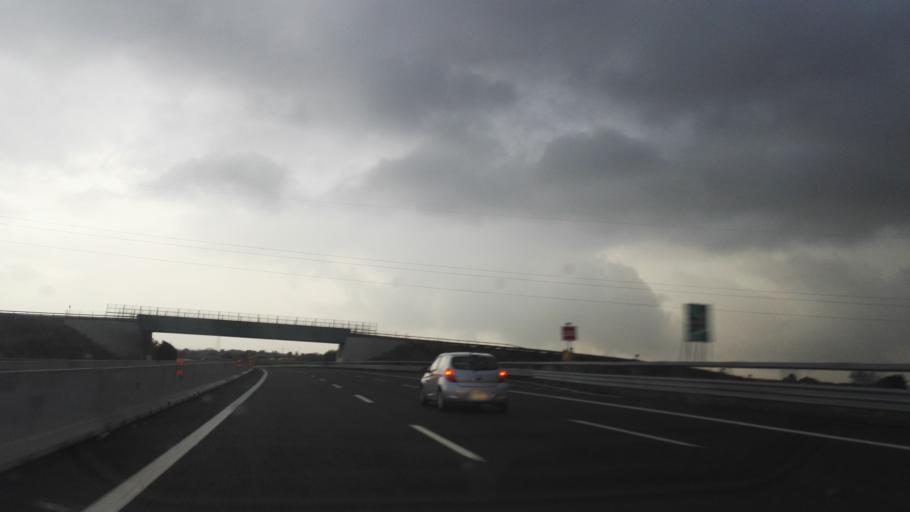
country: IT
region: Lombardy
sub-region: Citta metropolitana di Milano
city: Bellinzago Lombardo
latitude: 45.5322
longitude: 9.4388
